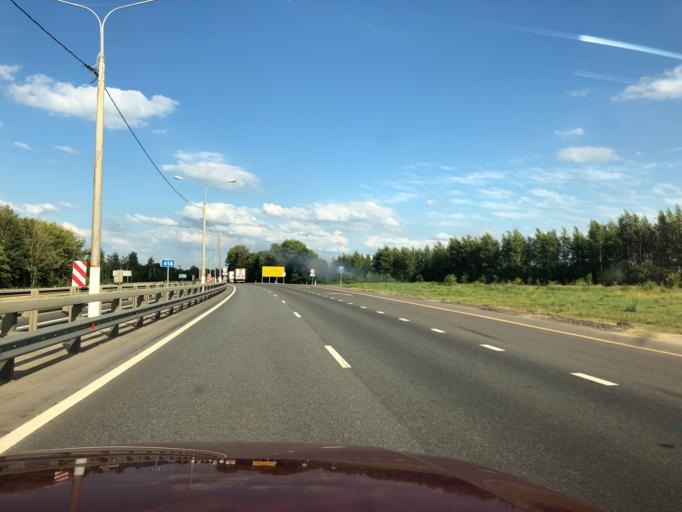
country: RU
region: Lipetsk
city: Zadonsk
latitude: 52.4420
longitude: 38.7950
